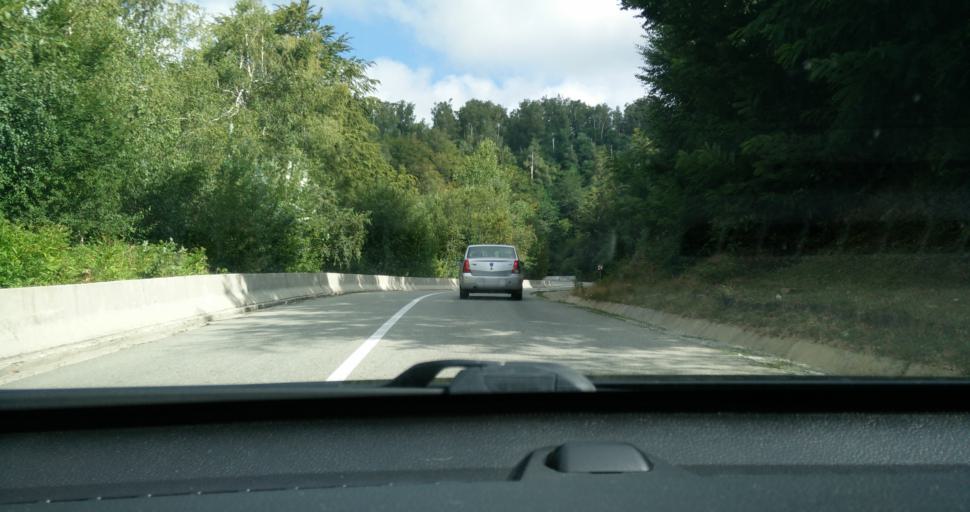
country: RO
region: Gorj
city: Novaci-Straini
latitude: 45.2066
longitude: 23.6982
